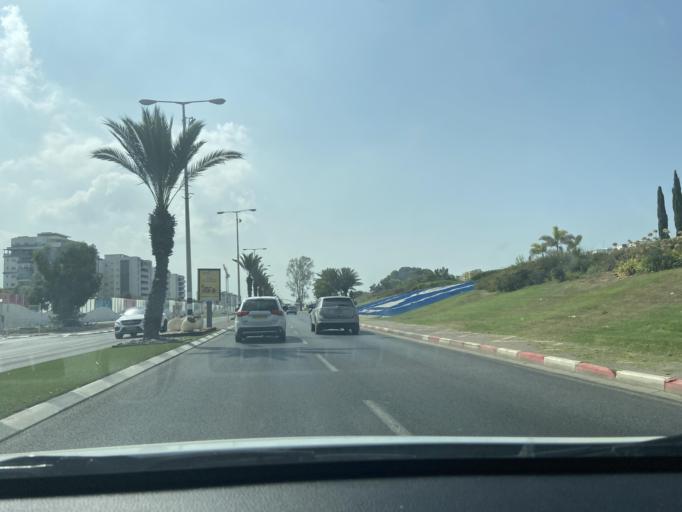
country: IL
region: Northern District
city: Nahariya
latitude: 33.0025
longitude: 35.0987
